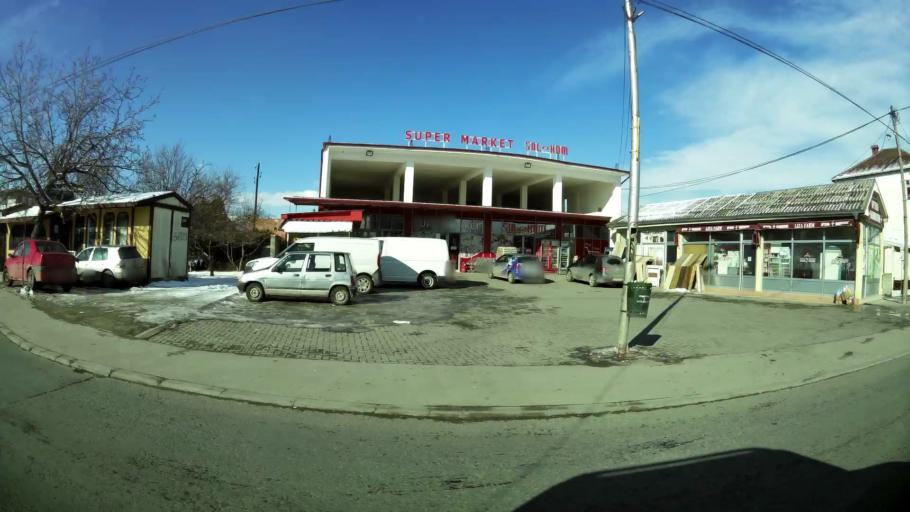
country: MK
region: Saraj
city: Saraj
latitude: 42.0001
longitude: 21.3287
